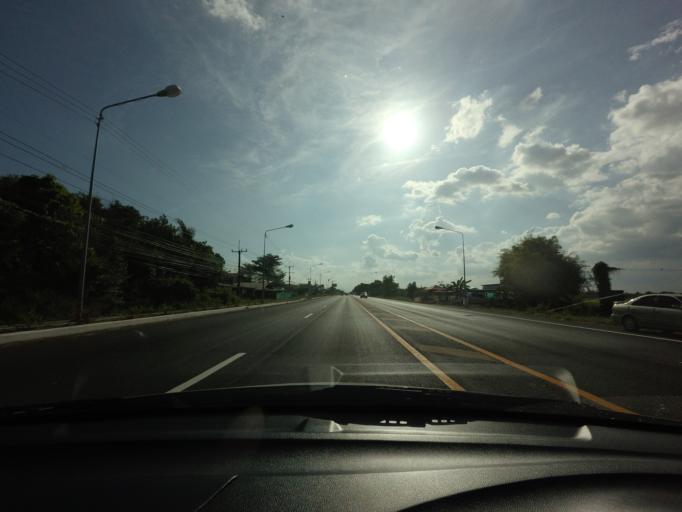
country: TH
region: Nakhon Nayok
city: Nakhon Nayok
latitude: 14.2382
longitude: 101.2452
